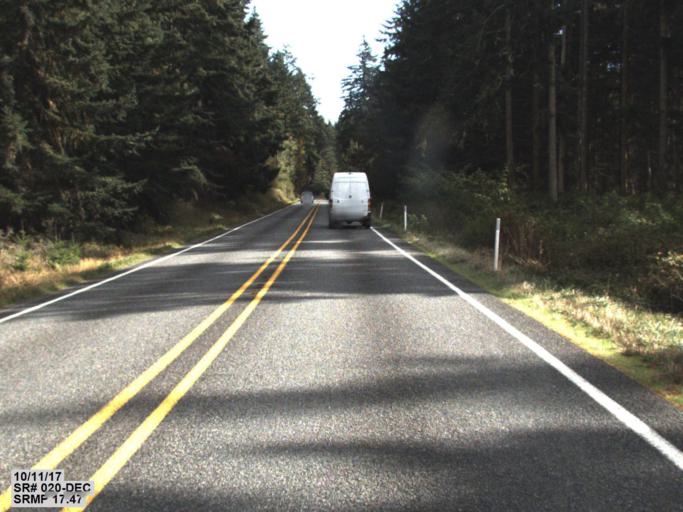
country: US
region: Washington
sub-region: Island County
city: Coupeville
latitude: 48.1825
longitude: -122.6252
